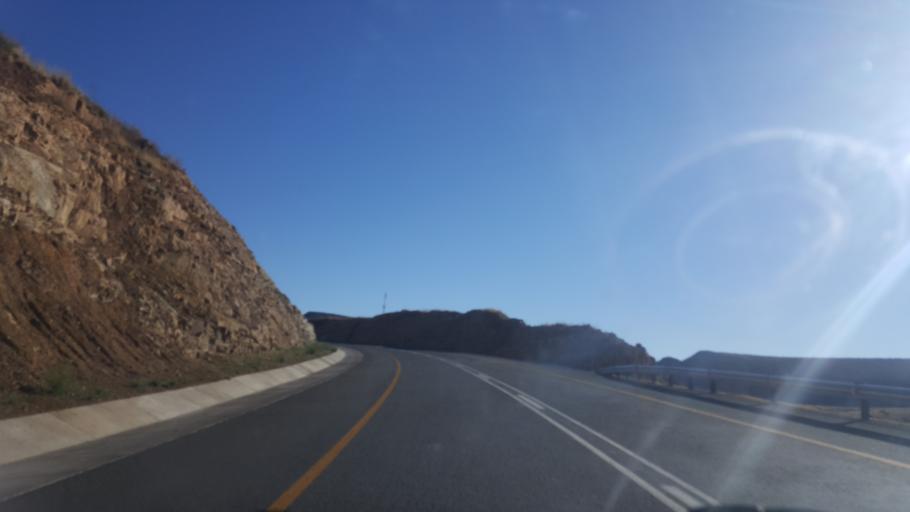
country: ZA
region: Eastern Cape
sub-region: Chris Hani District Municipality
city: Middelburg
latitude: -31.3804
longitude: 25.0341
